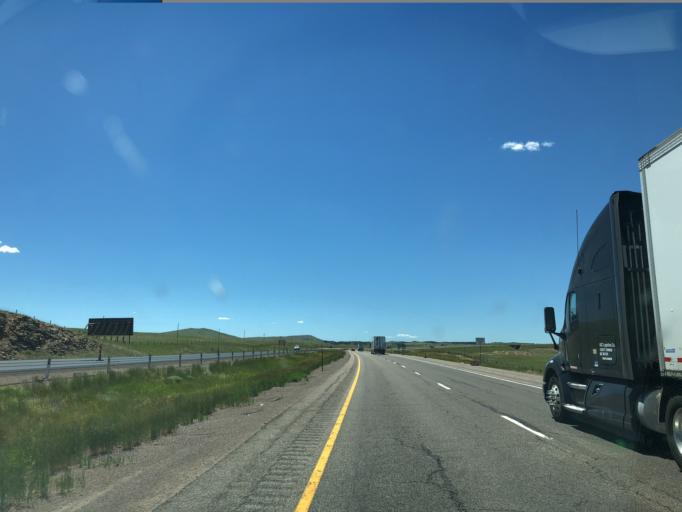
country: US
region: Wyoming
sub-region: Laramie County
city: Cheyenne
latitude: 41.0962
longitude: -105.1916
